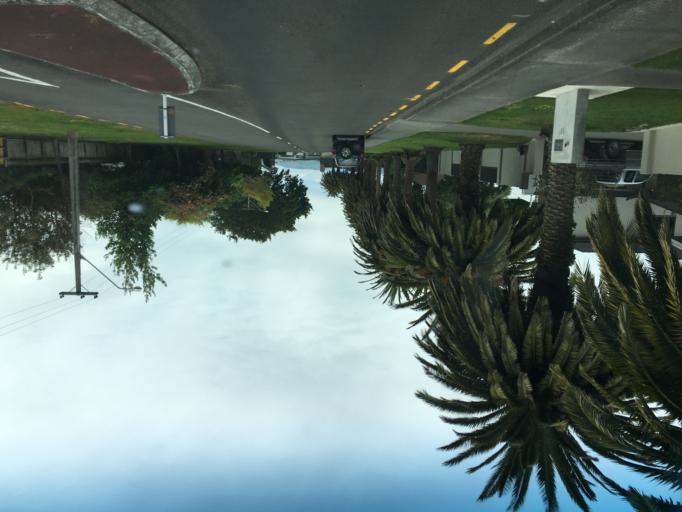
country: NZ
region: Manawatu-Wanganui
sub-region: Palmerston North City
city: Palmerston North
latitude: -40.3778
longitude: 175.5787
